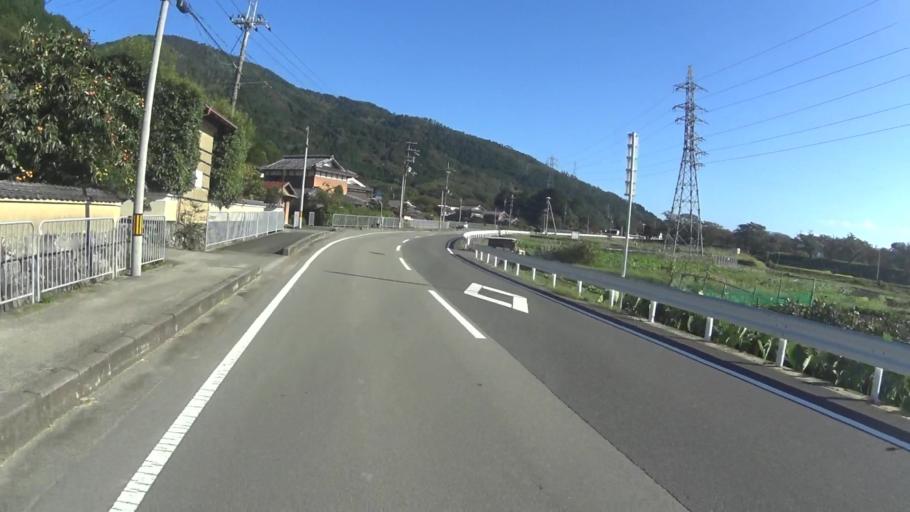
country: JP
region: Kyoto
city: Kameoka
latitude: 35.0479
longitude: 135.5826
